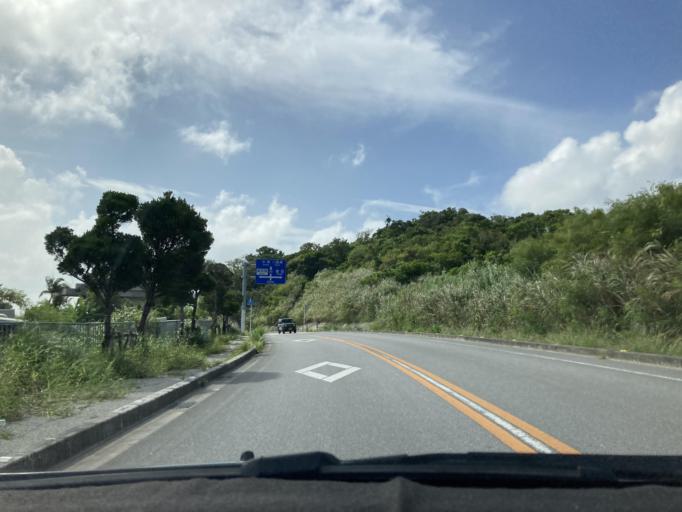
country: JP
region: Okinawa
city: Tomigusuku
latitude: 26.1406
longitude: 127.7698
